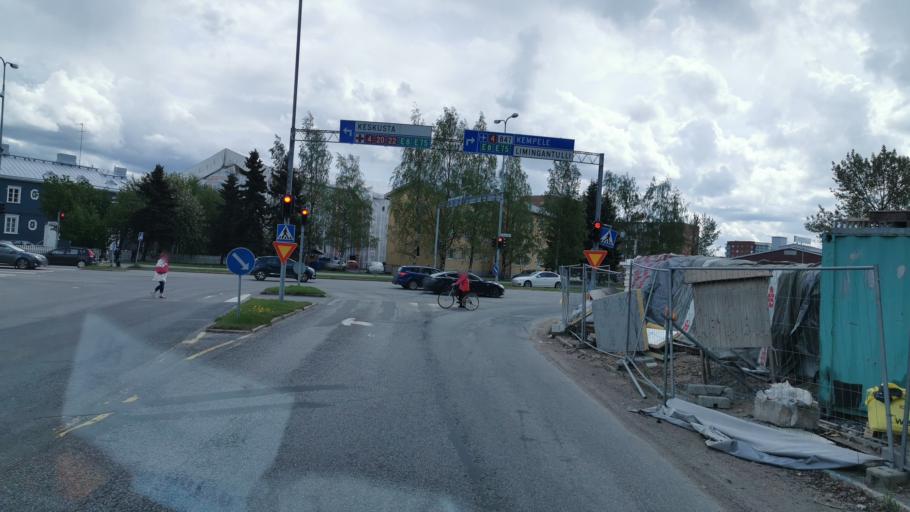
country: FI
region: Northern Ostrobothnia
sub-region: Oulu
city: Oulu
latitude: 65.0041
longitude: 25.4630
